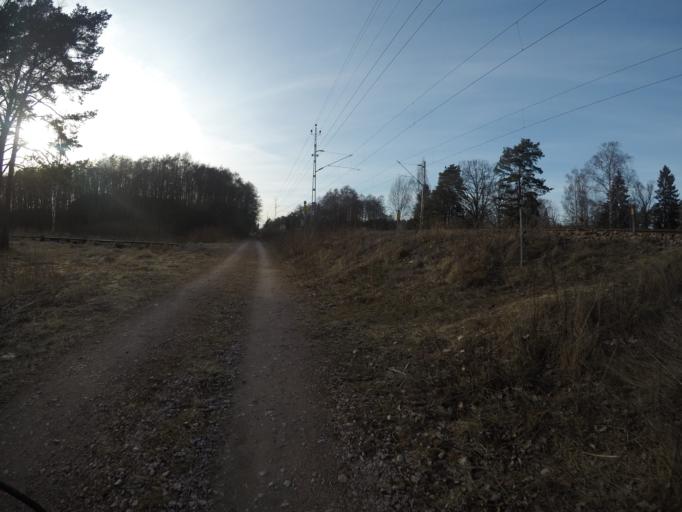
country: SE
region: Soedermanland
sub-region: Eskilstuna Kommun
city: Kvicksund
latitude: 59.4574
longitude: 16.3118
